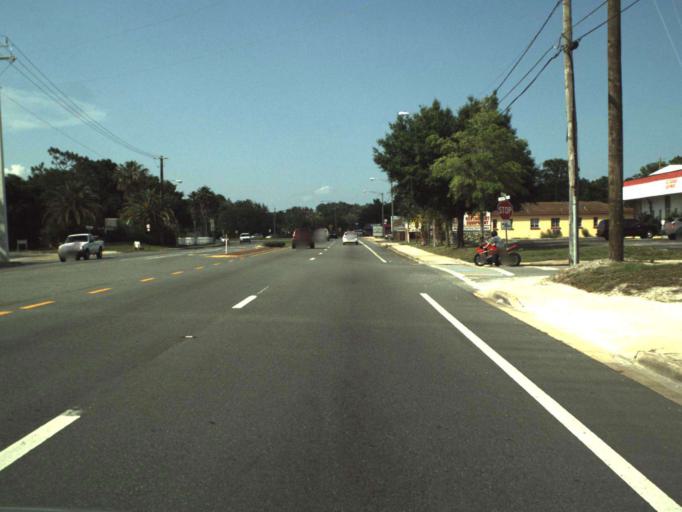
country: US
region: Florida
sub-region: Seminole County
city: Sanford
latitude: 28.7794
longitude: -81.2742
